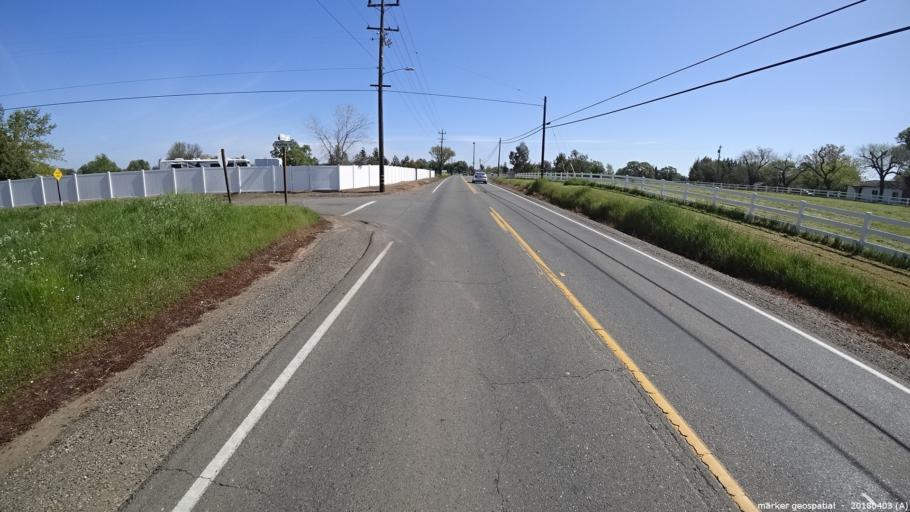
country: US
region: California
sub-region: Sacramento County
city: Wilton
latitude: 38.4239
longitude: -121.2127
